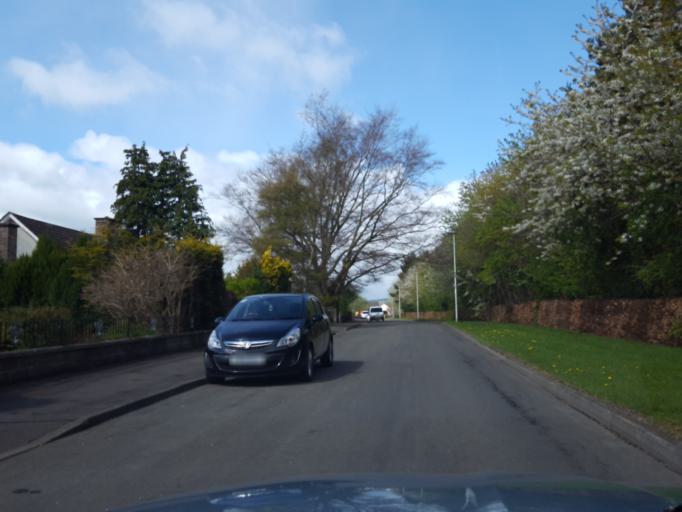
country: GB
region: Scotland
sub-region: Angus
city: Muirhead
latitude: 56.4620
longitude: -3.0575
